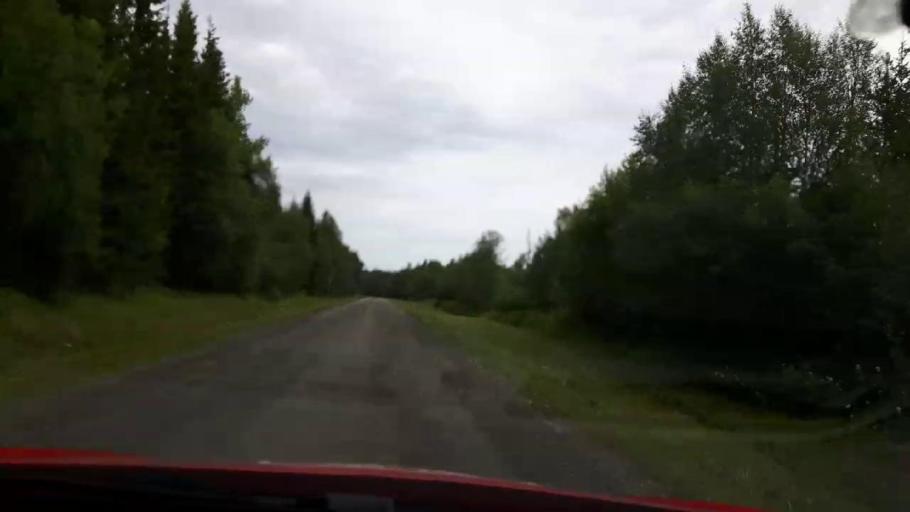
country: SE
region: Jaemtland
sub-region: Stroemsunds Kommun
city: Stroemsund
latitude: 63.7511
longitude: 15.5935
